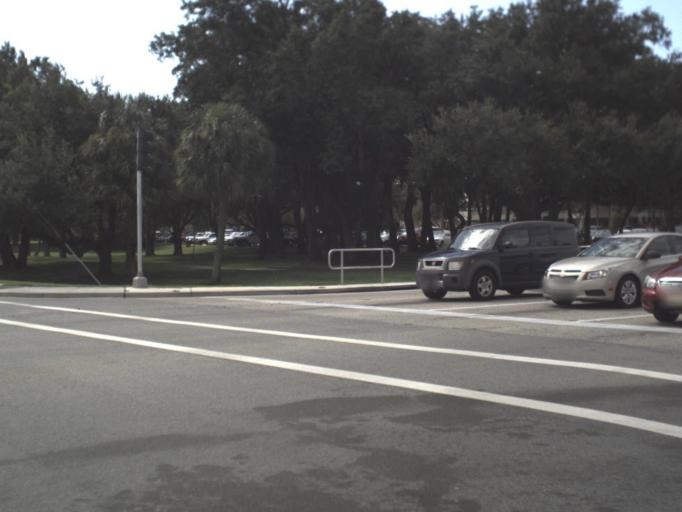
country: US
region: Florida
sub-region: Charlotte County
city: Port Charlotte
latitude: 27.0105
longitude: -82.1412
